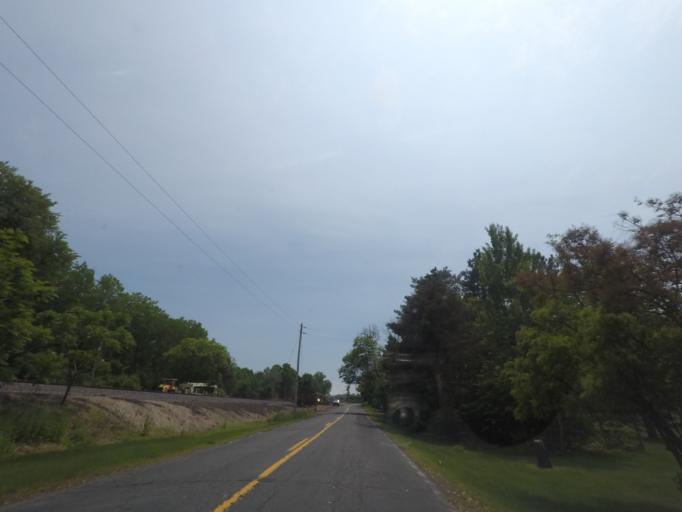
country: US
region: New York
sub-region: Rensselaer County
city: Castleton-on-Hudson
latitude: 42.4899
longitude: -73.6978
